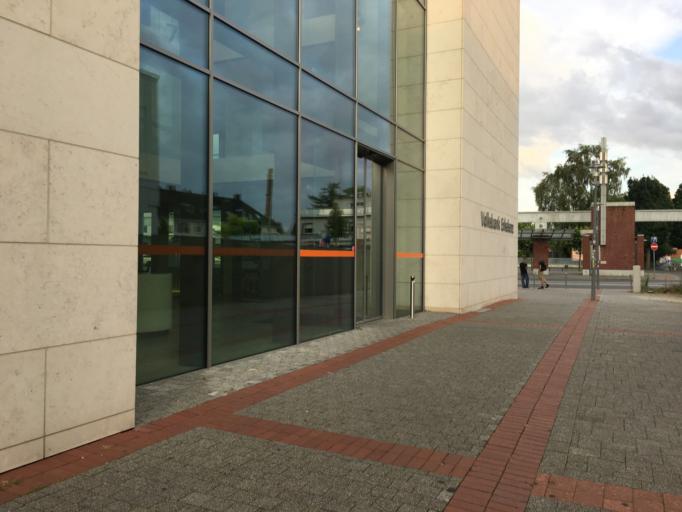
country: DE
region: North Rhine-Westphalia
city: Erkelenz
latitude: 51.0766
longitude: 6.3197
